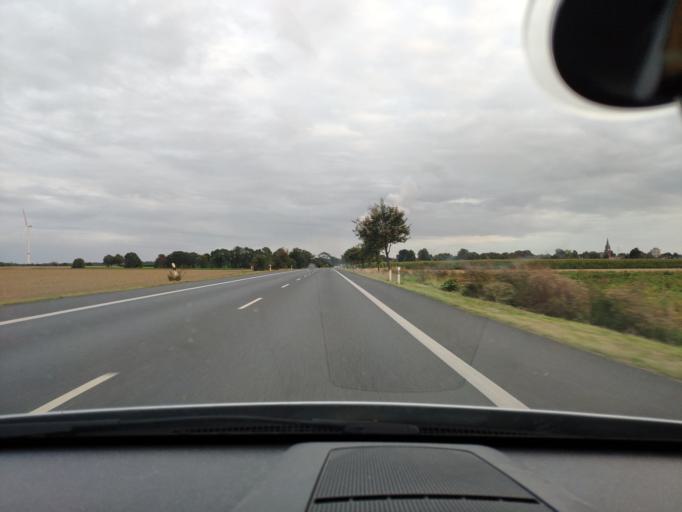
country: DE
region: North Rhine-Westphalia
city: Siersdorf
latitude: 50.9135
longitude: 6.2541
